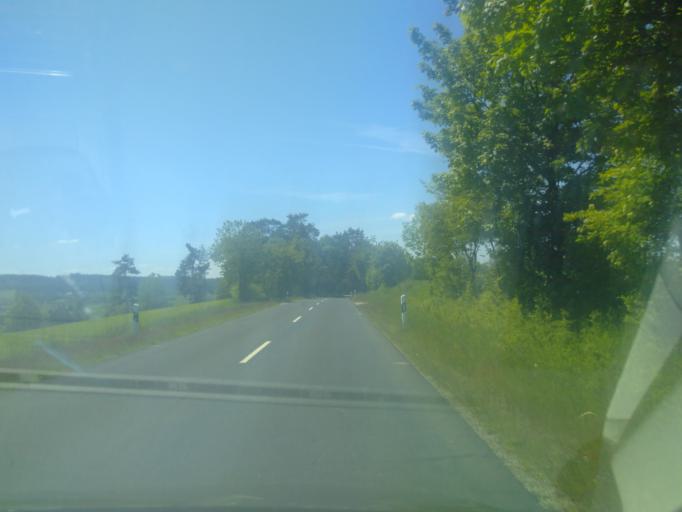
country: DE
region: Bavaria
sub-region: Upper Palatinate
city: Schwarzenbach
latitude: 49.8148
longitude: 12.3822
